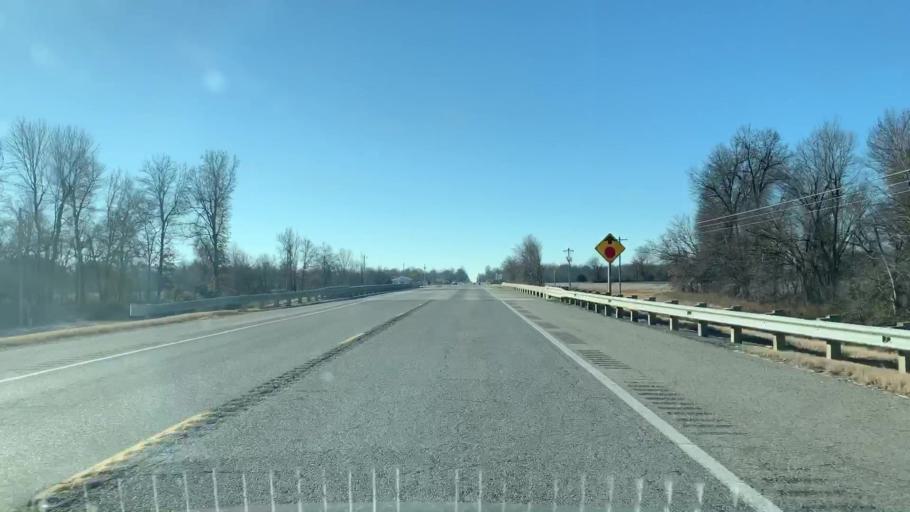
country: US
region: Kansas
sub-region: Cherokee County
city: Galena
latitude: 37.1834
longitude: -94.7046
